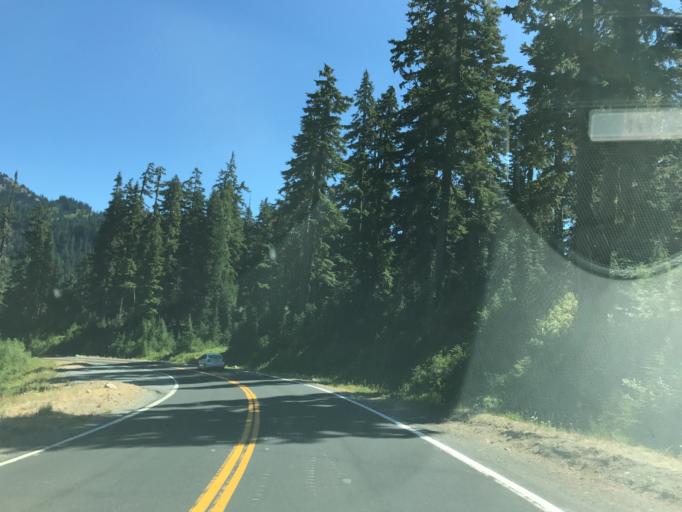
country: US
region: Washington
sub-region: King County
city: Enumclaw
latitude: 46.8655
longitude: -121.5398
